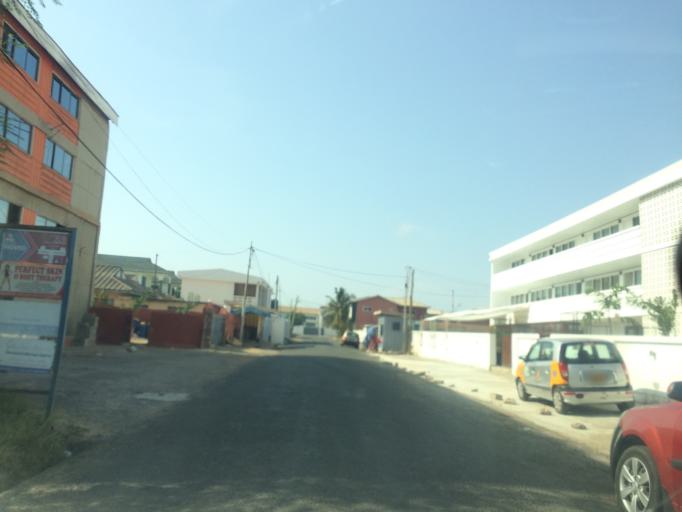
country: GH
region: Greater Accra
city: Accra
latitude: 5.5573
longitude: -0.1715
